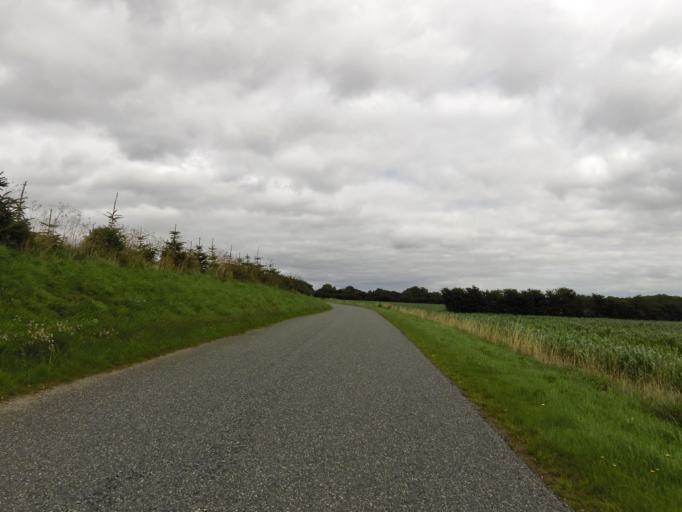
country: DK
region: South Denmark
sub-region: Haderslev Kommune
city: Gram
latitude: 55.2977
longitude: 9.1630
